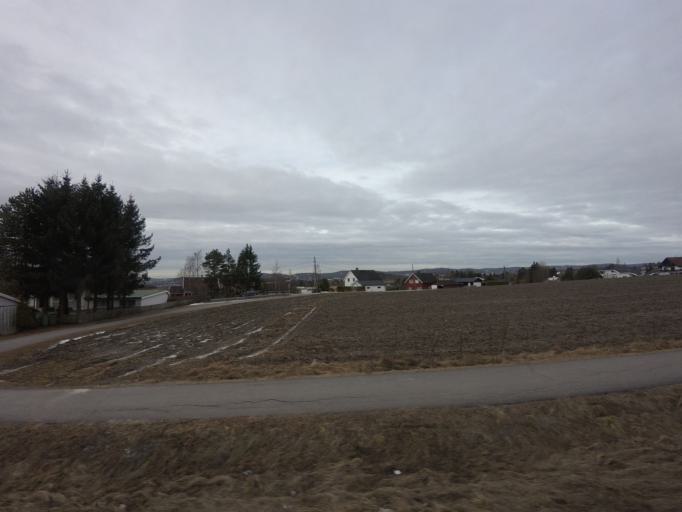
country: NO
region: Akershus
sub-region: Skedsmo
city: Lillestrom
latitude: 59.9849
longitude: 11.0493
